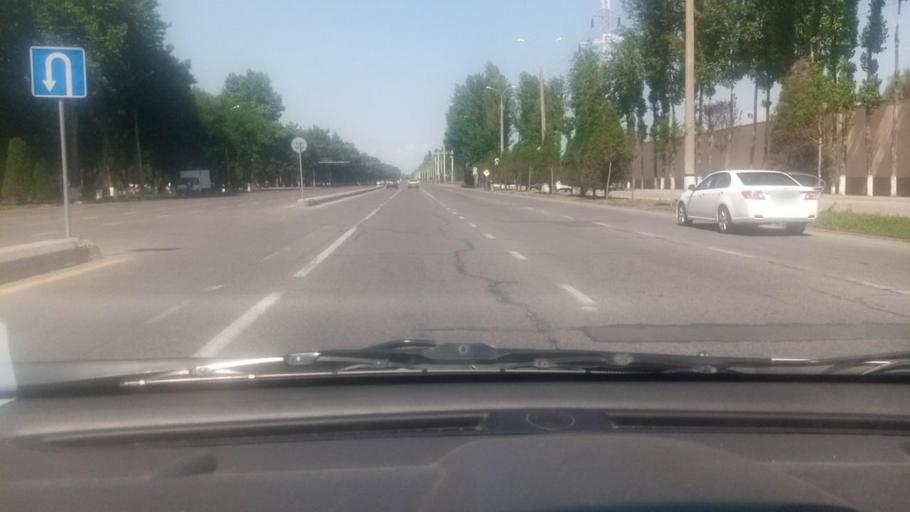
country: UZ
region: Toshkent
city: Salor
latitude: 41.3220
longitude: 69.3634
